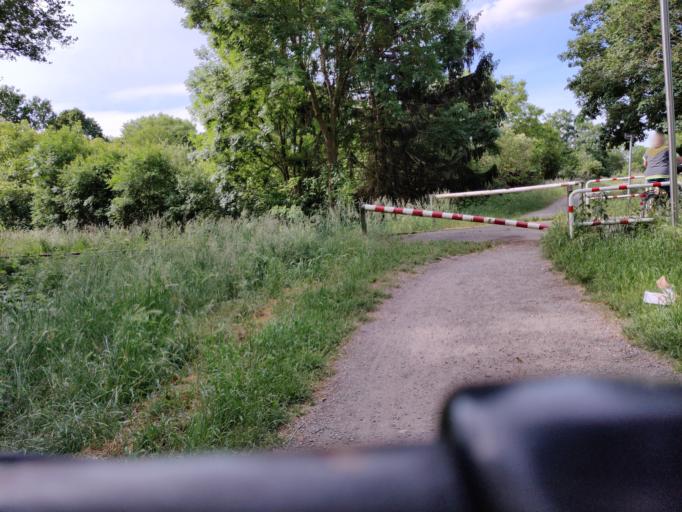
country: DE
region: Lower Saxony
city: Wunstorf
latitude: 52.4308
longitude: 9.4376
